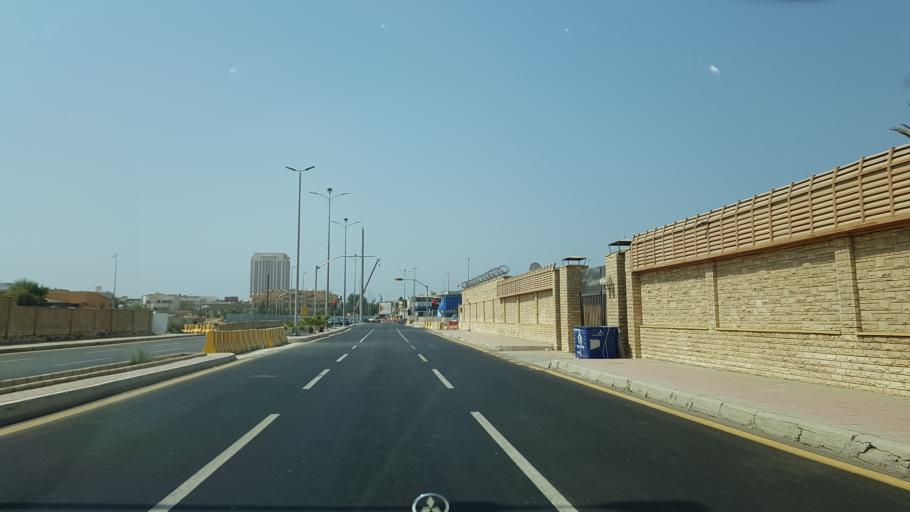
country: SA
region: Makkah
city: Jeddah
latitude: 21.5297
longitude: 39.1623
